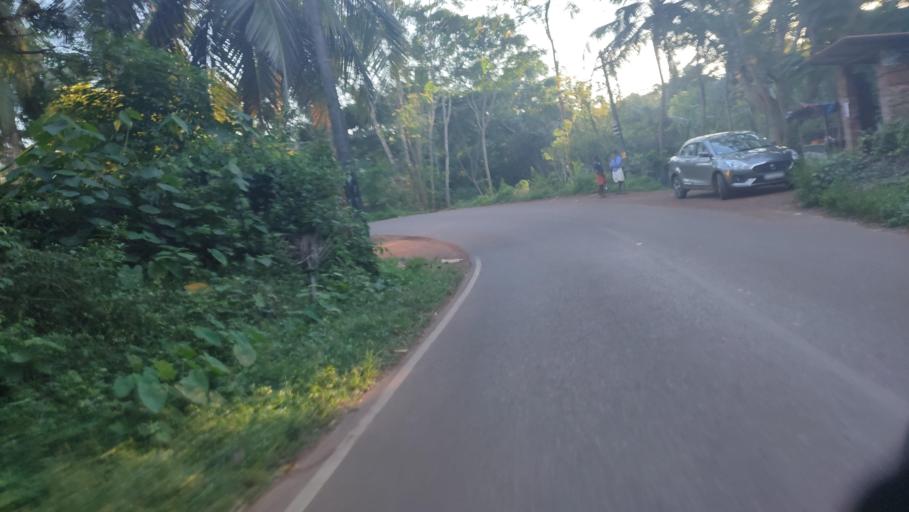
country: IN
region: Kerala
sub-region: Kasaragod District
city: Kannangad
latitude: 12.4016
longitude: 75.0635
